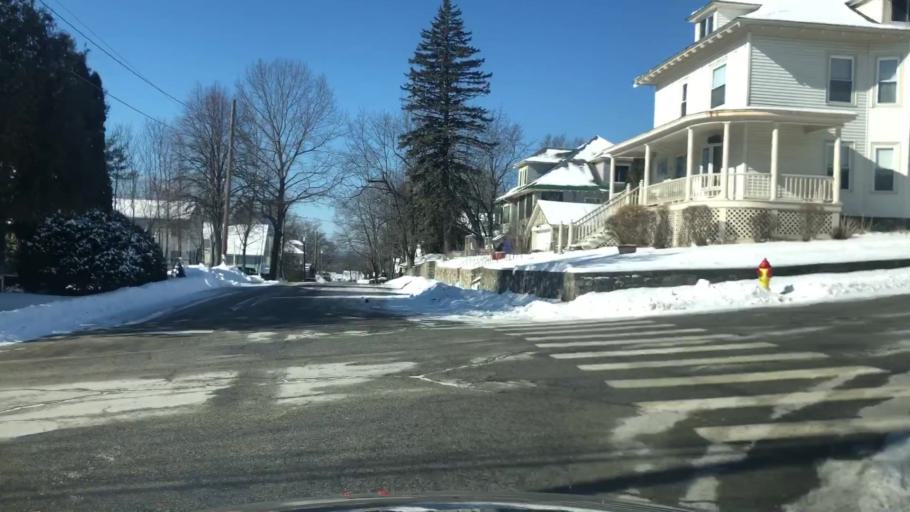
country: US
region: New Hampshire
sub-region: Hillsborough County
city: Manchester
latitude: 42.9912
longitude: -71.4393
